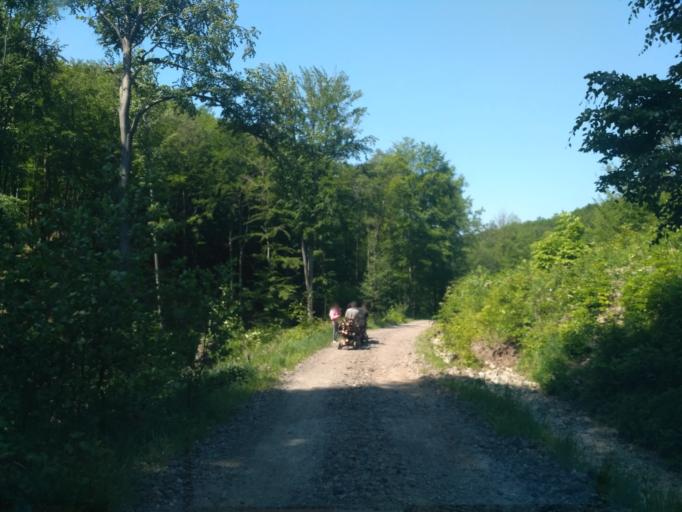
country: SK
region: Presovsky
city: Vranov nad Topl'ou
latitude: 48.8373
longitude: 21.4649
